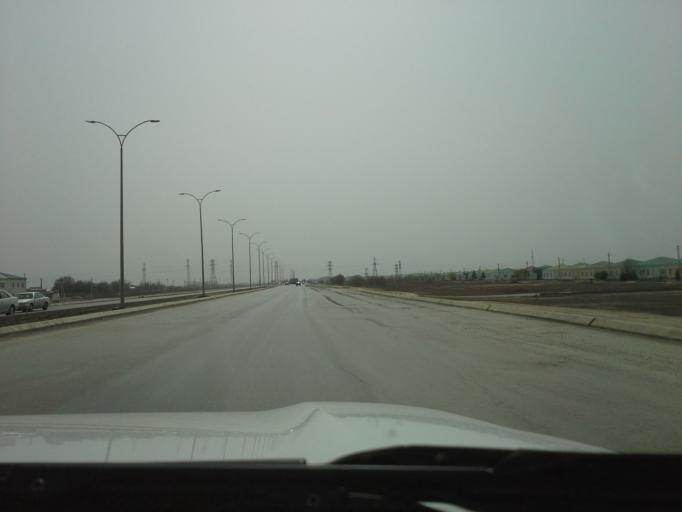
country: TM
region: Ahal
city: Tejen
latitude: 37.3725
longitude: 60.5204
